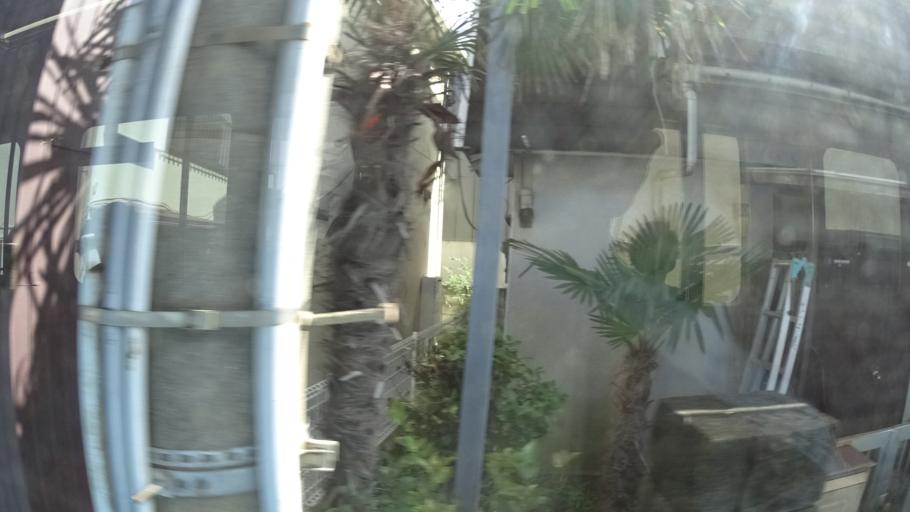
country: JP
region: Kanagawa
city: Fujisawa
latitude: 35.3081
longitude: 139.4937
